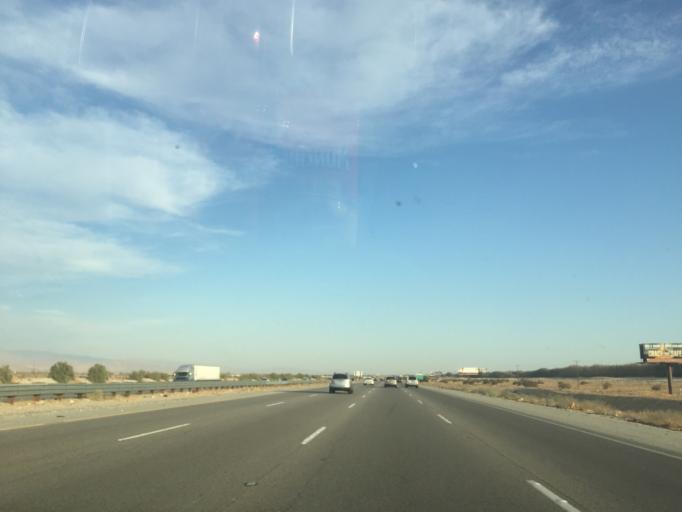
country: US
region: California
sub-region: Riverside County
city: Thousand Palms
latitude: 33.8355
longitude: -116.4350
